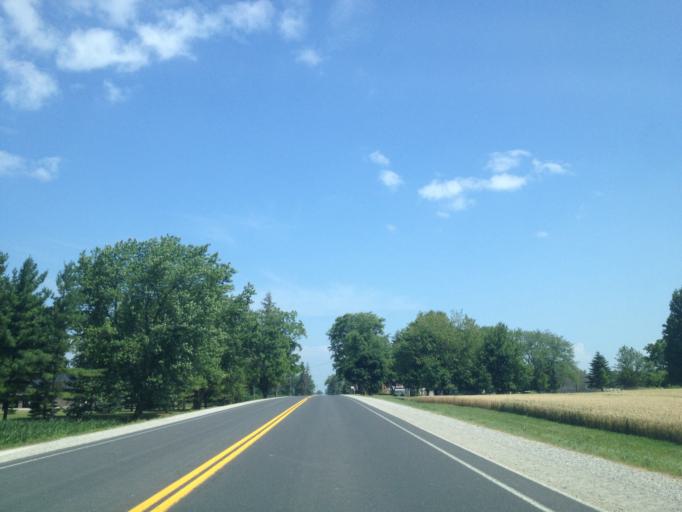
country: CA
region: Ontario
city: Stratford
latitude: 43.3144
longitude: -81.2018
